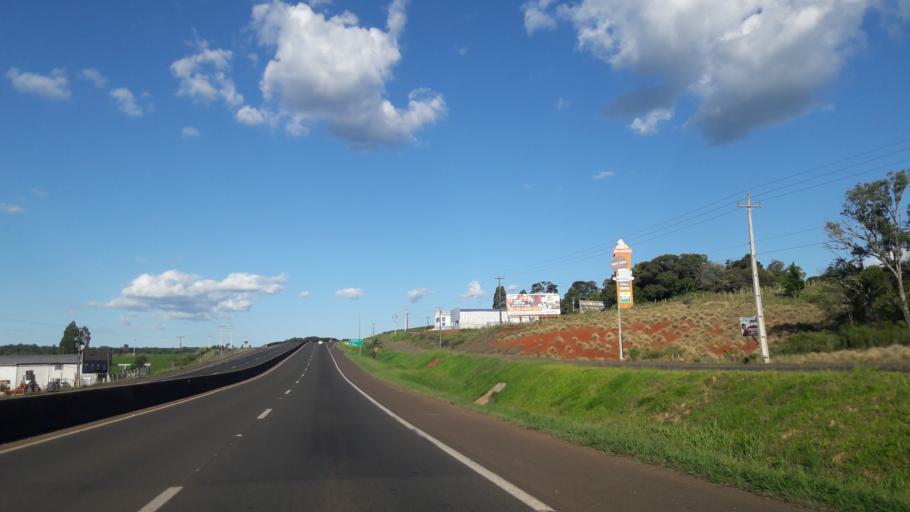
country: BR
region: Parana
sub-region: Guarapuava
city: Guarapuava
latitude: -25.3421
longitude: -51.4339
